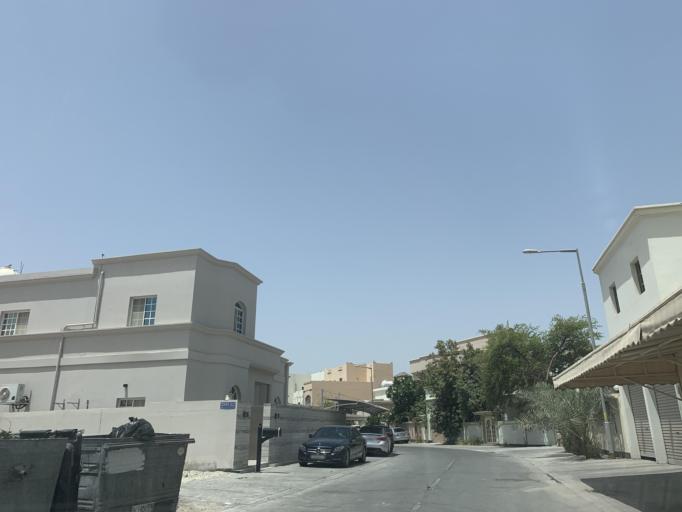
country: BH
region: Northern
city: Madinat `Isa
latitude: 26.1629
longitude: 50.5775
